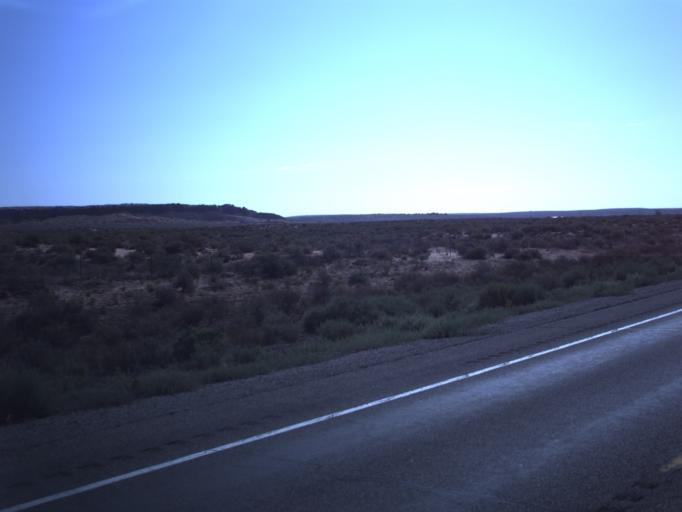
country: US
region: Utah
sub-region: San Juan County
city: Blanding
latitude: 37.1901
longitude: -109.5956
